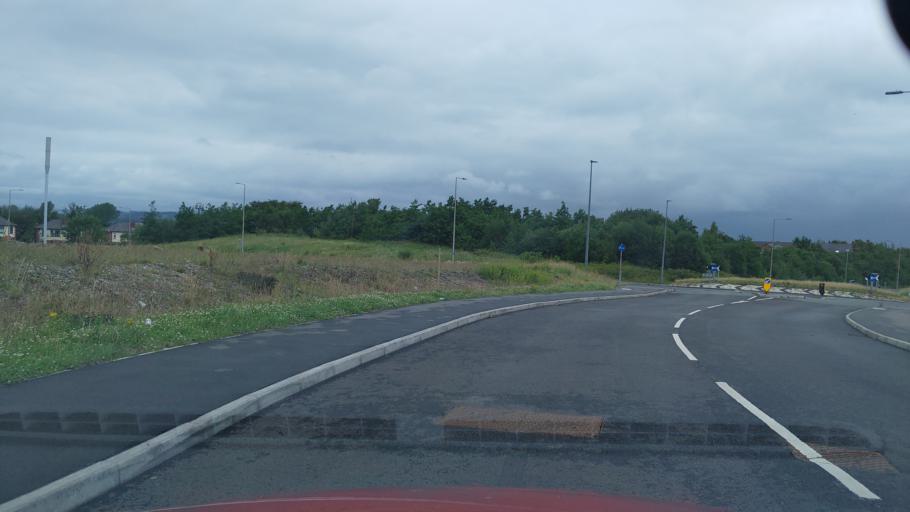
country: GB
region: England
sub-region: Borough of Wigan
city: Ince-in-Makerfield
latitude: 53.5292
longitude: -2.6631
